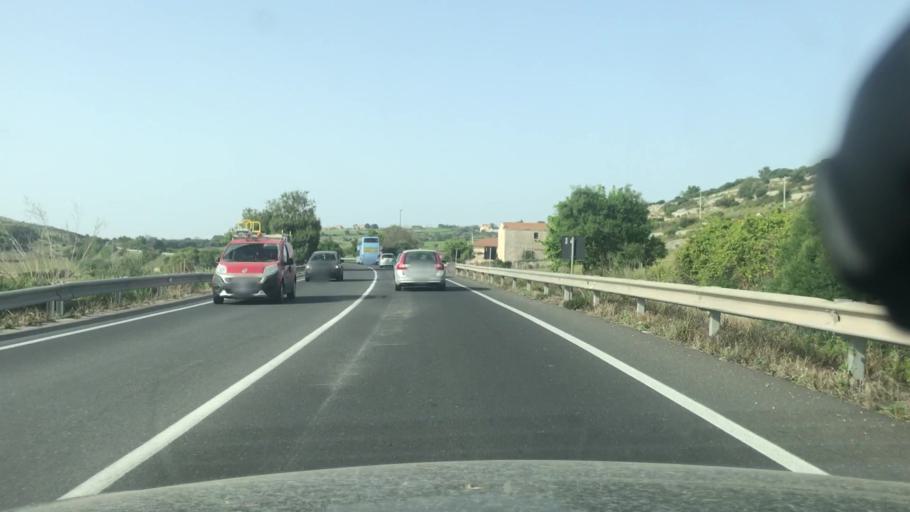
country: IT
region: Sicily
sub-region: Ragusa
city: Ragusa
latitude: 36.8732
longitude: 14.6903
